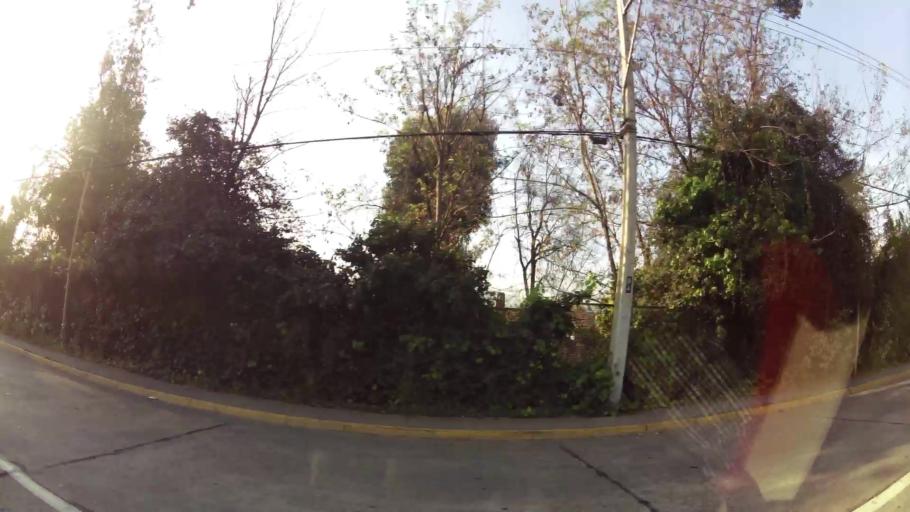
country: CL
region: Santiago Metropolitan
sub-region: Provincia de Santiago
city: Villa Presidente Frei, Nunoa, Santiago, Chile
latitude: -33.3926
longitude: -70.5358
